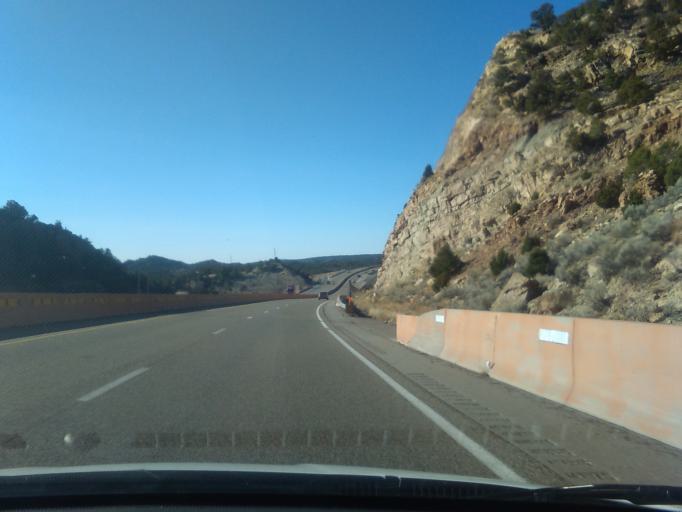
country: US
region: New Mexico
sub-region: Santa Fe County
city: Eldorado at Santa Fe
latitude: 35.5520
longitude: -105.8219
